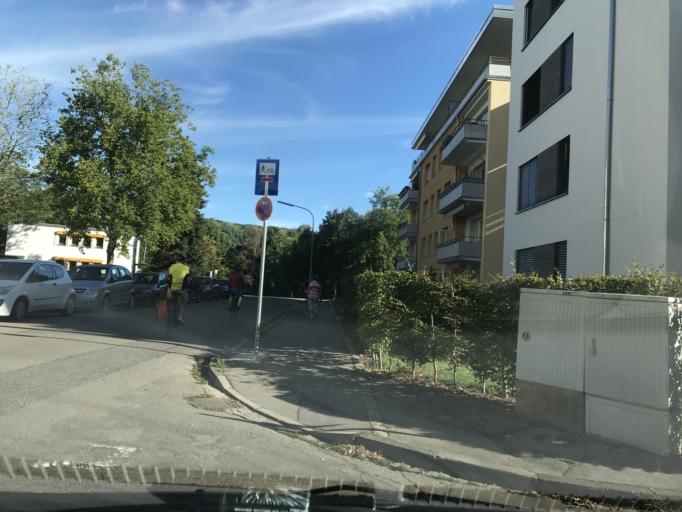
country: DE
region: Baden-Wuerttemberg
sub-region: Freiburg Region
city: Loerrach
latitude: 47.6244
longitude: 7.6676
